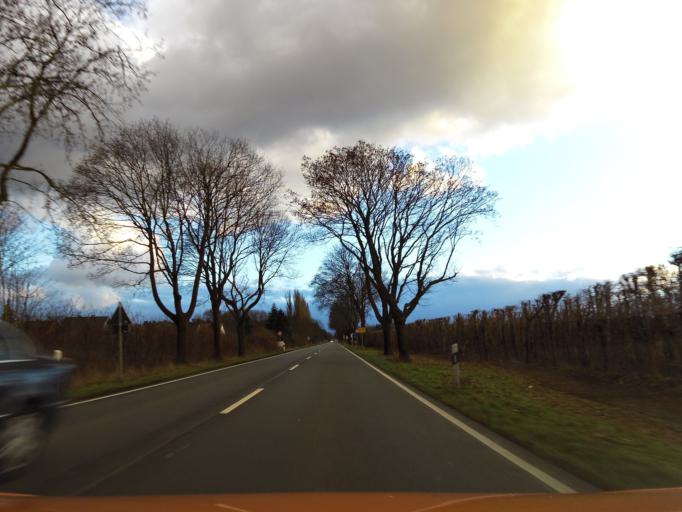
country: DE
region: Lower Saxony
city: Didderse
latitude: 52.3718
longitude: 10.3857
